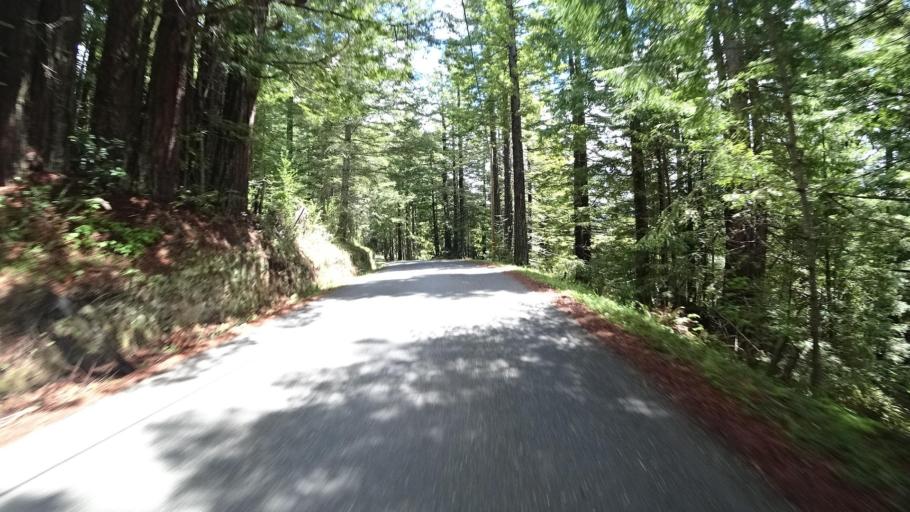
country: US
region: California
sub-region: Humboldt County
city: Blue Lake
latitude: 40.8446
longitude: -123.9236
